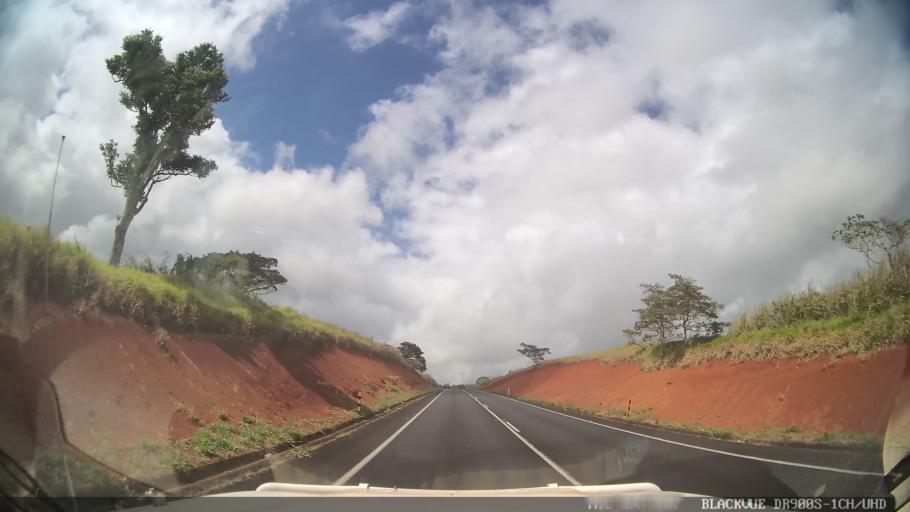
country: AU
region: Queensland
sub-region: Tablelands
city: Atherton
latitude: -17.2982
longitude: 145.6193
